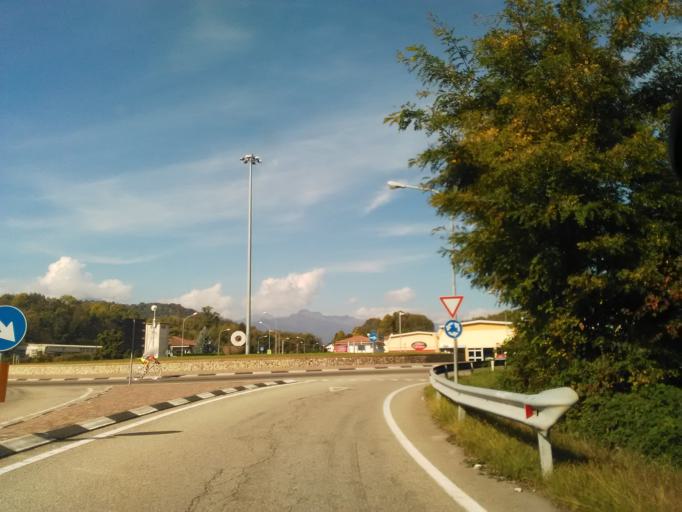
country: IT
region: Piedmont
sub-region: Provincia di Novara
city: Grignasco
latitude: 45.6716
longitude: 8.3251
